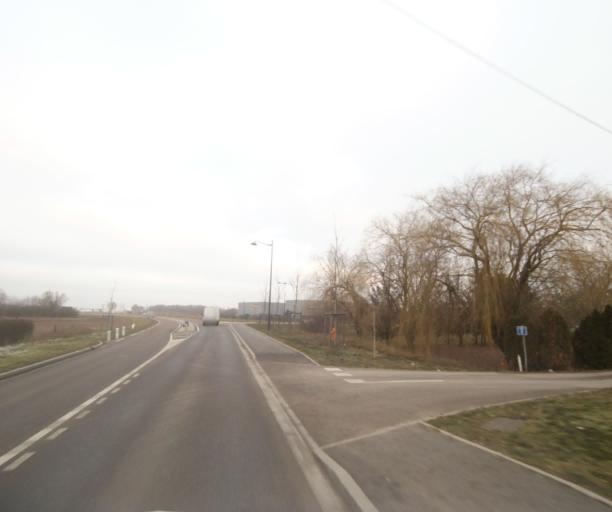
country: FR
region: Champagne-Ardenne
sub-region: Departement de la Haute-Marne
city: Bettancourt-la-Ferree
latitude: 48.6492
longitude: 4.9546
